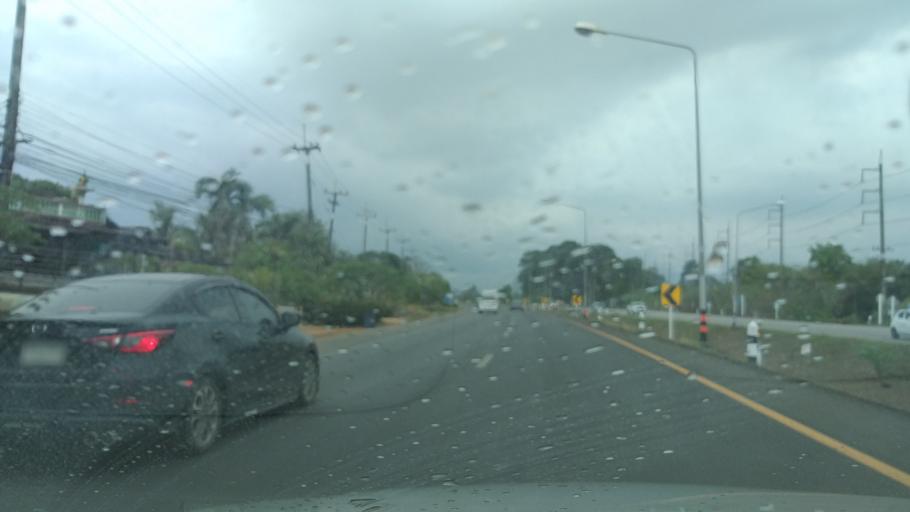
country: TH
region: Chanthaburi
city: Khlung
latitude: 12.4293
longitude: 102.3145
